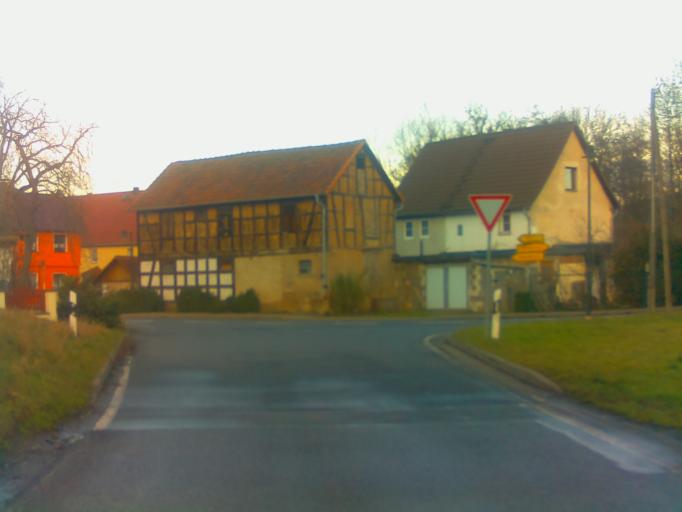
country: DE
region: Thuringia
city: Rudolstadt
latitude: 50.7147
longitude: 11.3942
